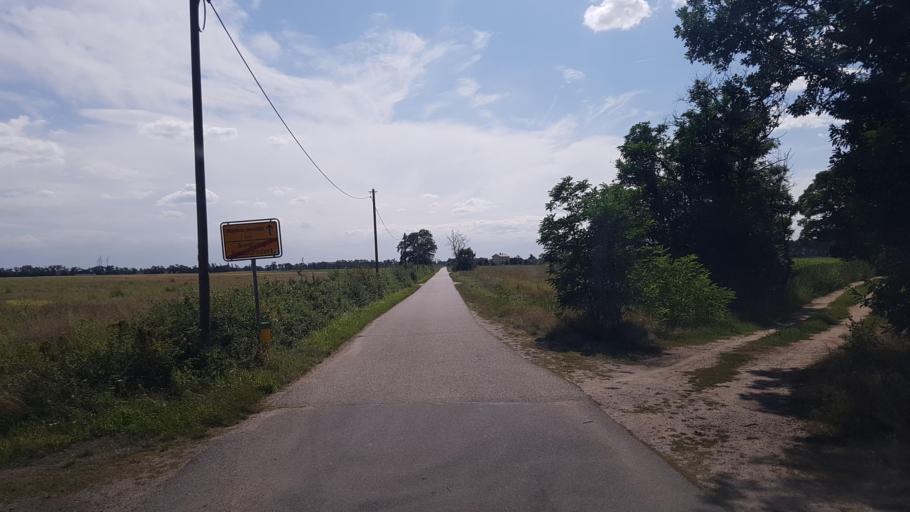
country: DE
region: Brandenburg
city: Muhlberg
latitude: 51.4448
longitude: 13.2908
